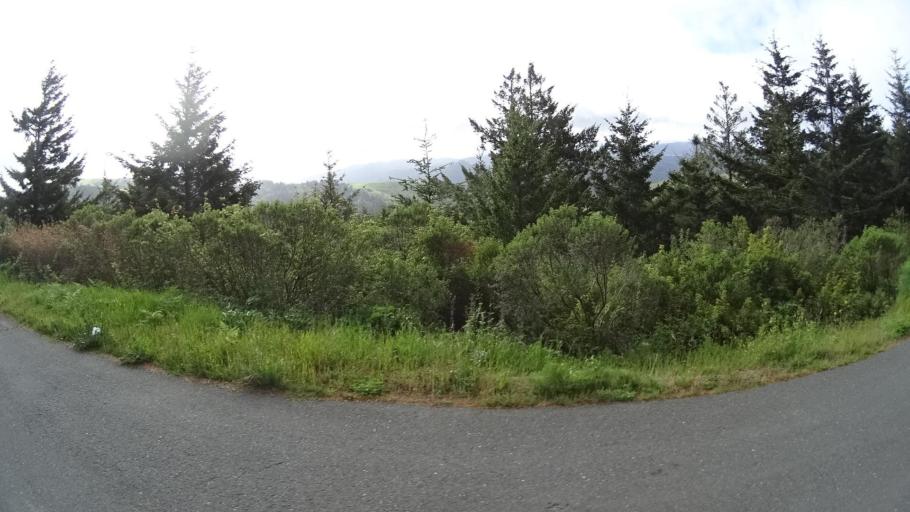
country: US
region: California
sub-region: Humboldt County
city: Ferndale
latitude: 40.4859
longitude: -124.3374
